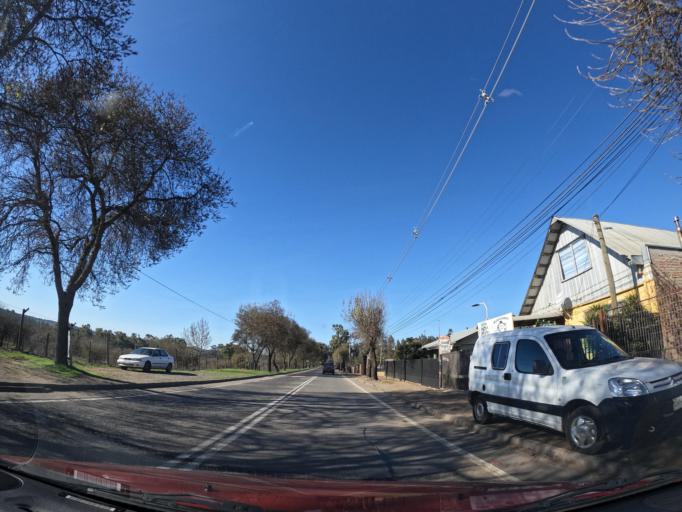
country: CL
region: Maule
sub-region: Provincia de Cauquenes
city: Cauquenes
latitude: -35.9579
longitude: -72.2964
